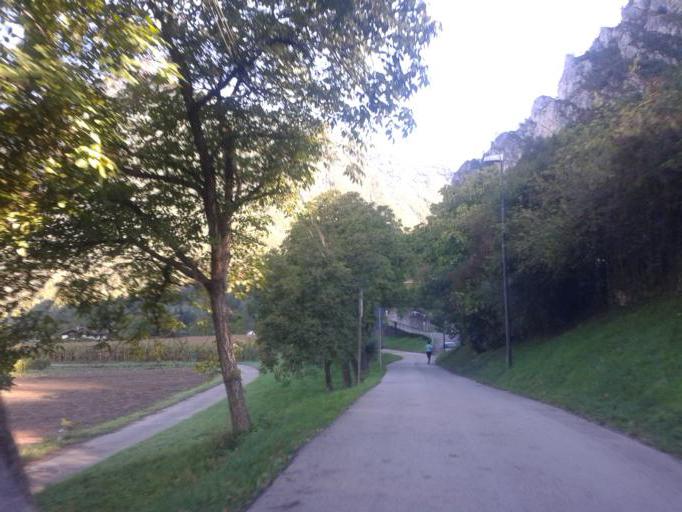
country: IT
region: Trentino-Alto Adige
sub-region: Provincia di Trento
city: Storo
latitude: 45.8540
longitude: 10.5765
